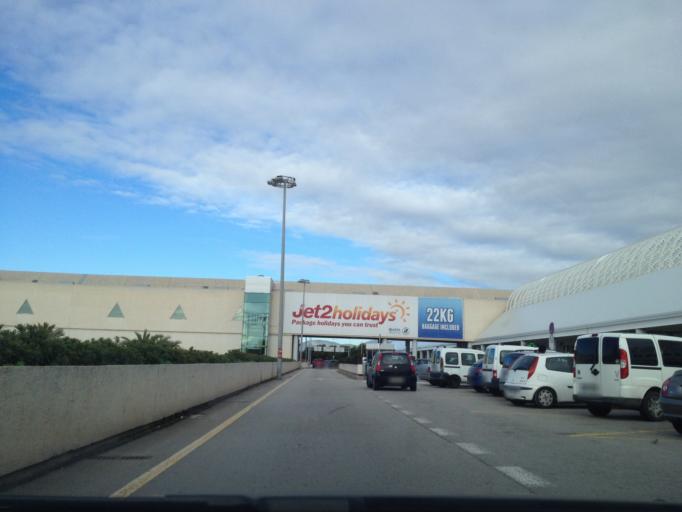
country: ES
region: Balearic Islands
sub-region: Illes Balears
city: s'Arenal
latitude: 39.5466
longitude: 2.7309
